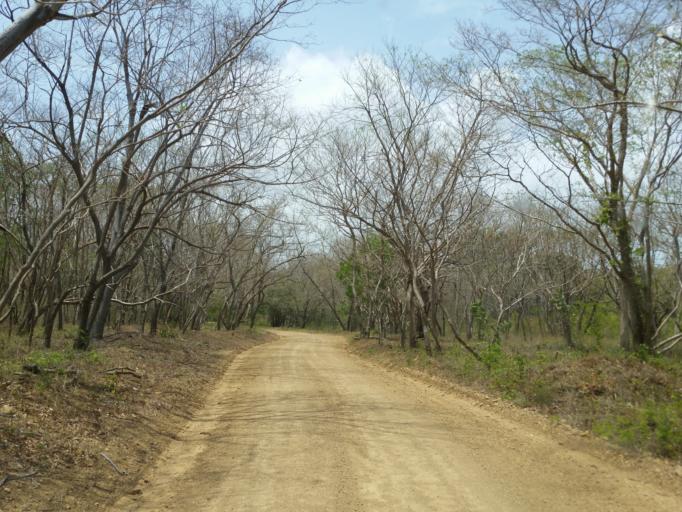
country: NI
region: Rivas
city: Tola
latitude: 11.4179
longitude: -86.0599
